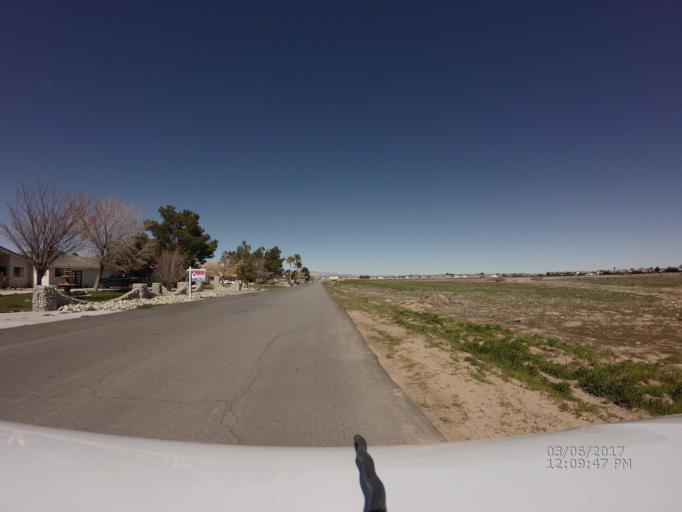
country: US
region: California
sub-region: Los Angeles County
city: Quartz Hill
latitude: 34.6753
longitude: -118.2059
